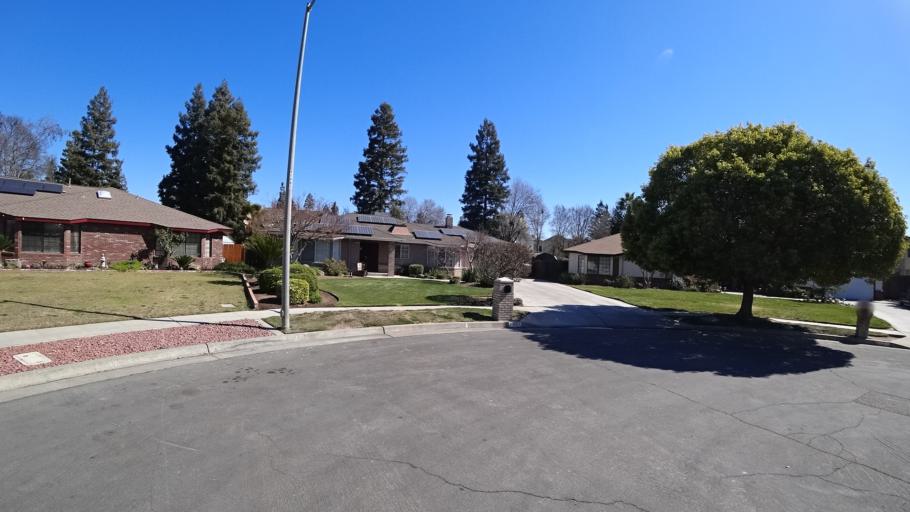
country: US
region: California
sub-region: Fresno County
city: Clovis
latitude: 36.8473
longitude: -119.7494
